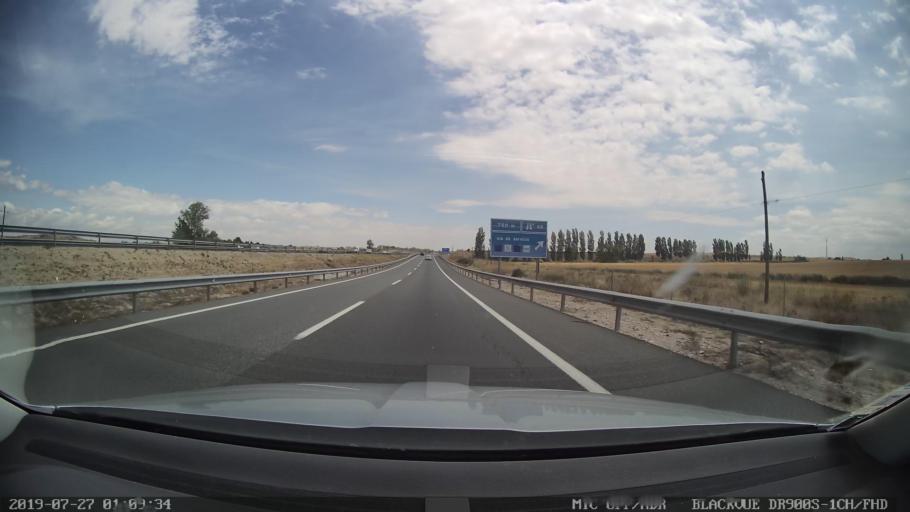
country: ES
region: Castille-La Mancha
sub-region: Province of Toledo
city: Otero
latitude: 40.0176
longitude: -4.5343
